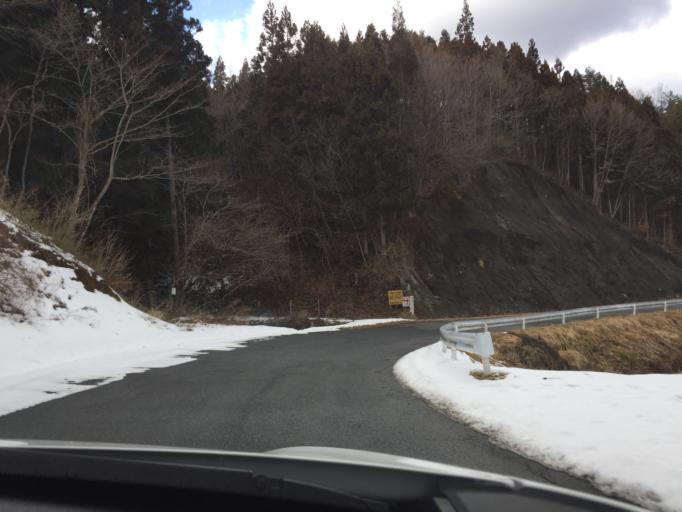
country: JP
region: Fukushima
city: Iwaki
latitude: 37.2245
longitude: 140.7421
